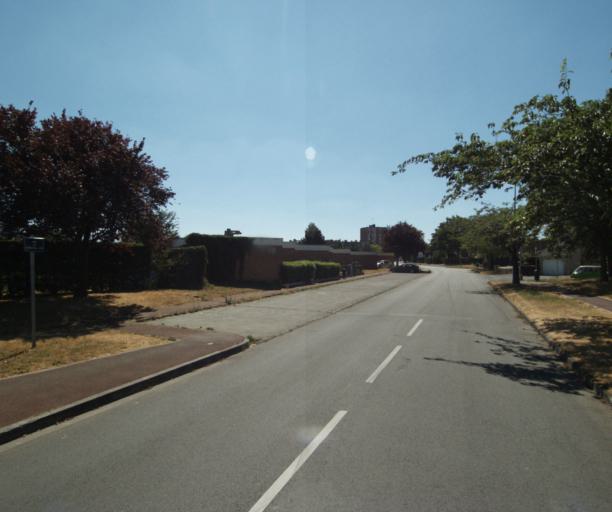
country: BE
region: Wallonia
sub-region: Province du Hainaut
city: Mouscron
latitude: 50.7396
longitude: 3.1862
